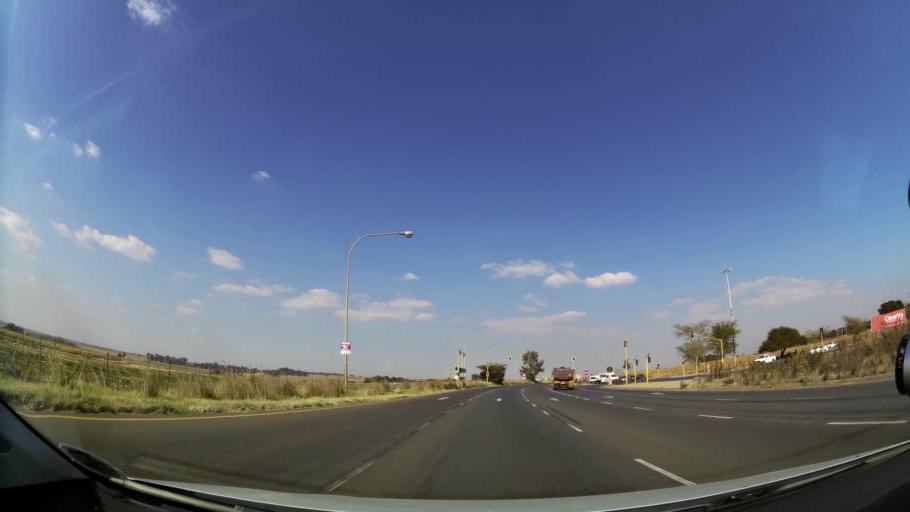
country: ZA
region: Gauteng
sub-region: Ekurhuleni Metropolitan Municipality
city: Tembisa
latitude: -26.0397
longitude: 28.2581
